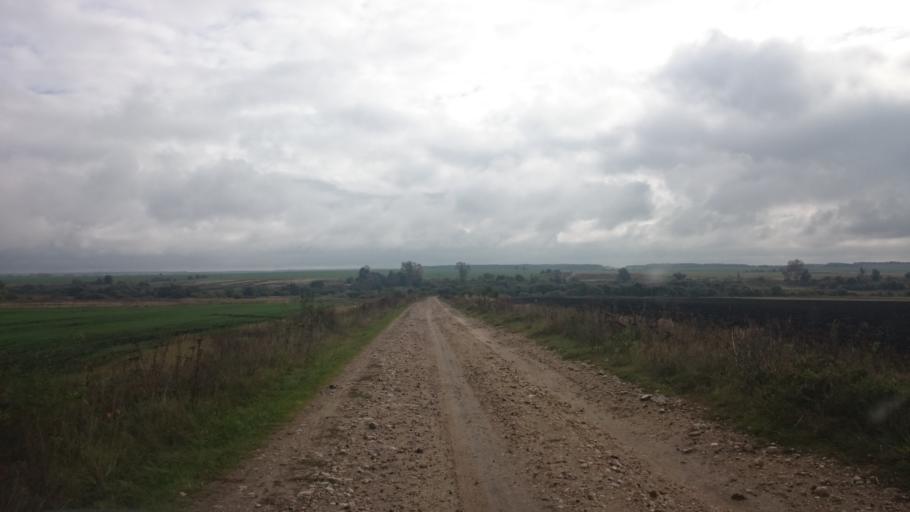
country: RU
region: Mordoviya
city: Kadoshkino
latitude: 54.0200
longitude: 44.4477
